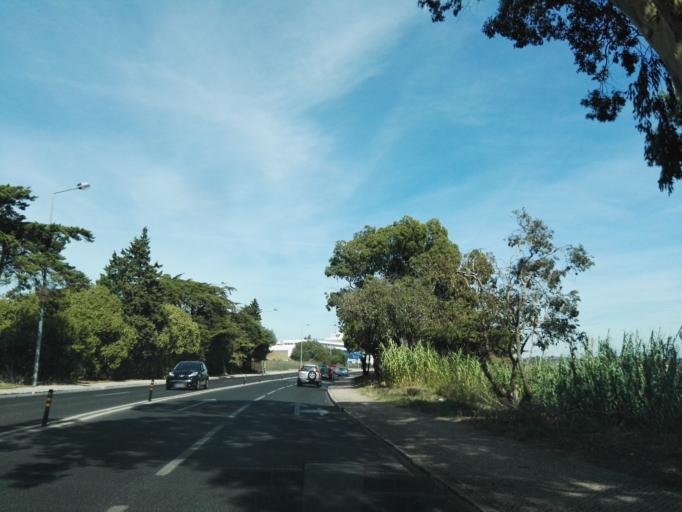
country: PT
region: Lisbon
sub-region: Oeiras
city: Oeiras
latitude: 38.6884
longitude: -9.3016
